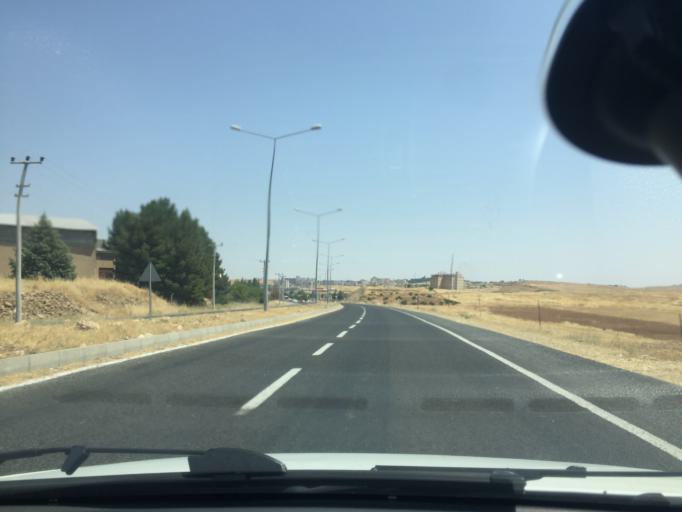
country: TR
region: Mardin
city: Acirli
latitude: 37.4380
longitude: 41.2991
